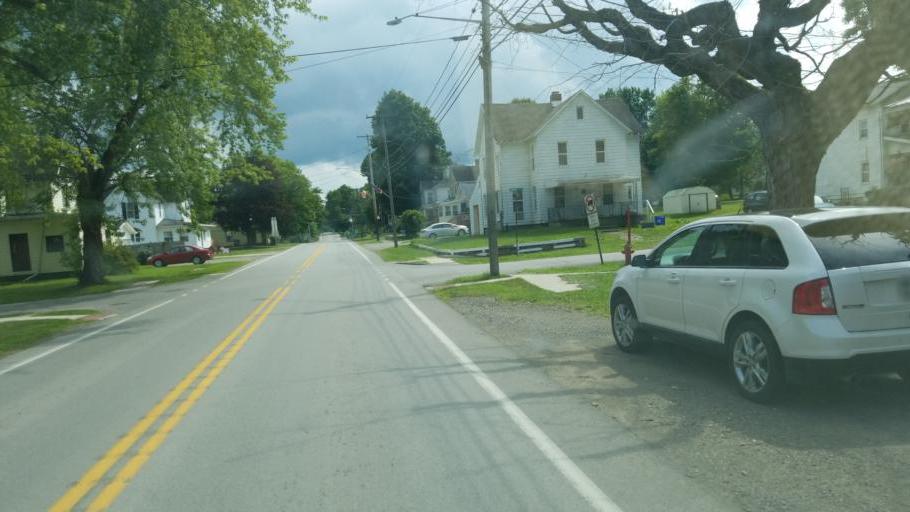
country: US
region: Pennsylvania
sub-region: Crawford County
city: Conneaut Lakeshore
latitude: 41.6024
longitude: -80.3044
